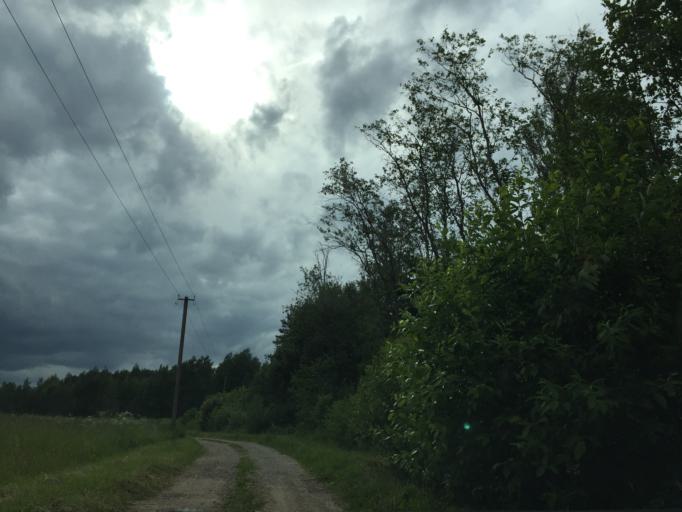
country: LV
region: Apes Novads
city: Ape
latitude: 57.4203
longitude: 26.3750
